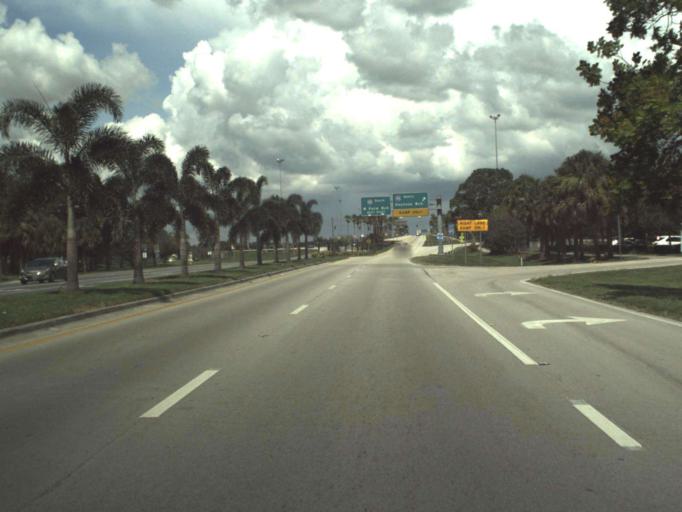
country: US
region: Florida
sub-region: Saint Lucie County
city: Port Saint Lucie
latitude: 27.3115
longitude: -80.4076
